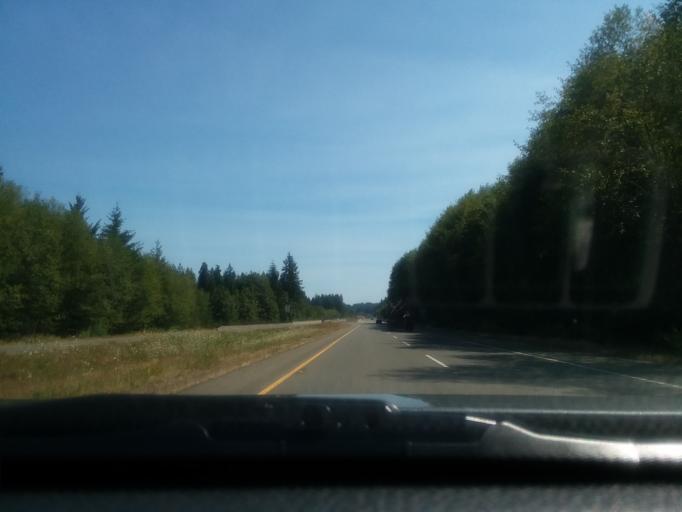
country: CA
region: British Columbia
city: Port Alberni
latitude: 49.4428
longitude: -124.7615
